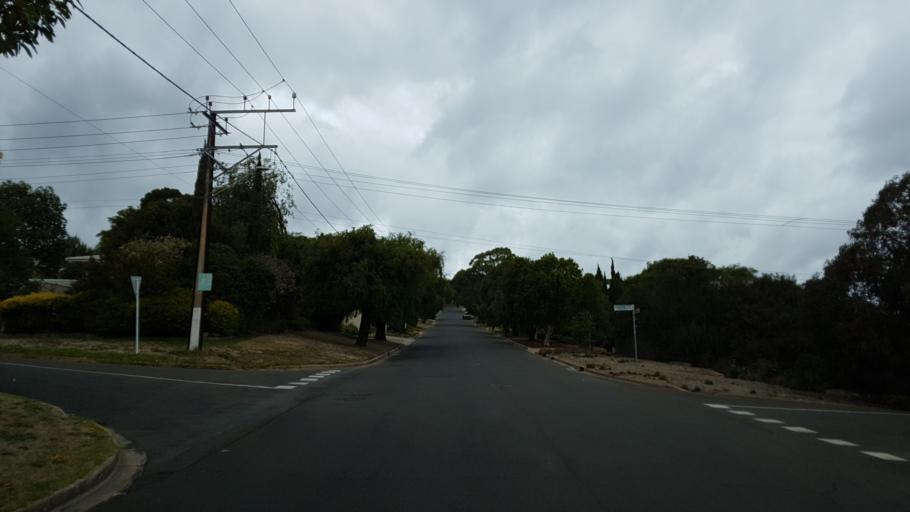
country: AU
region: South Australia
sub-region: Mitcham
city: Clapham
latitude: -35.0037
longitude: 138.5957
